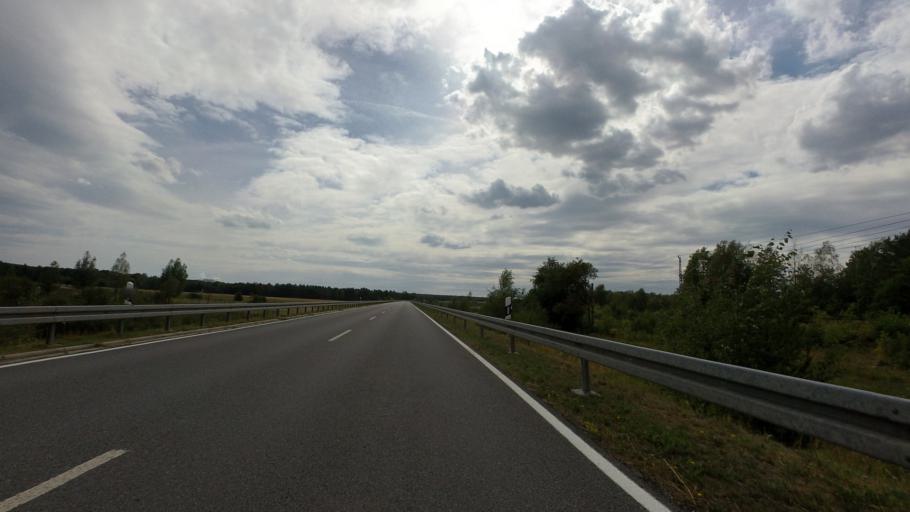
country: DE
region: Brandenburg
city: Spremberg
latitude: 51.5903
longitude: 14.3532
